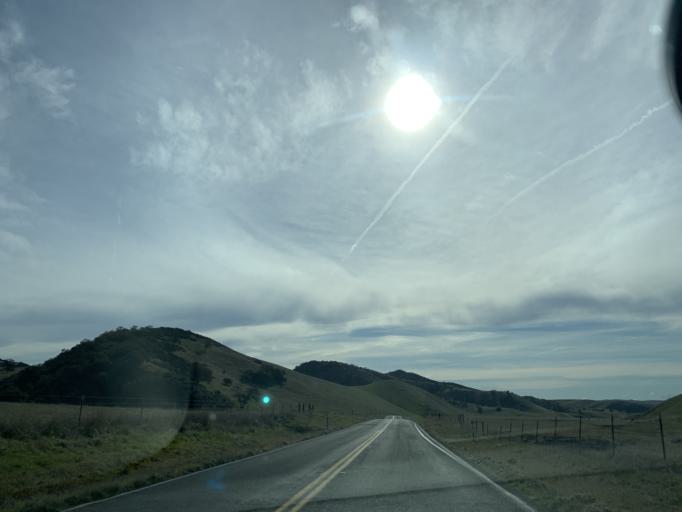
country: US
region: California
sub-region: Monterey County
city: Greenfield
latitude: 36.4554
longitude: -121.0506
